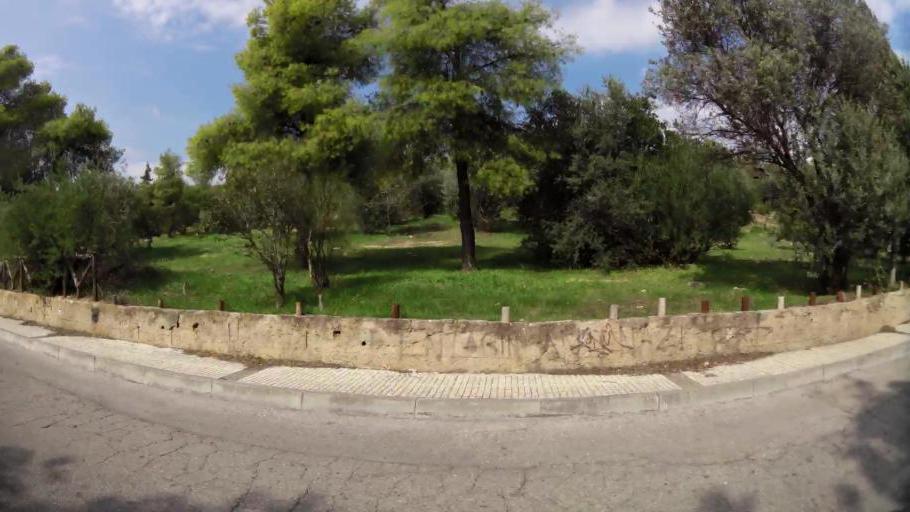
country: GR
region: Attica
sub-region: Nomarchia Athinas
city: Petroupolis
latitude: 38.0489
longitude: 23.6906
